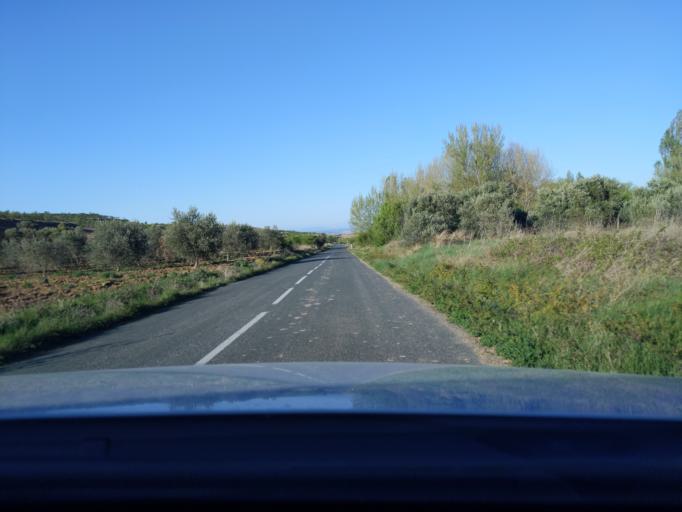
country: ES
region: La Rioja
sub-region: Provincia de La Rioja
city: Bergasa
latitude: 42.2600
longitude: -2.1112
